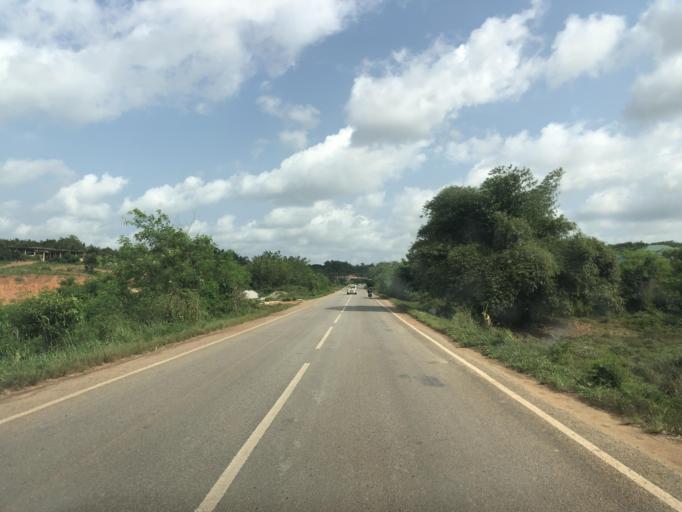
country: GH
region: Central
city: Cape Coast
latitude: 5.1927
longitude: -1.3173
